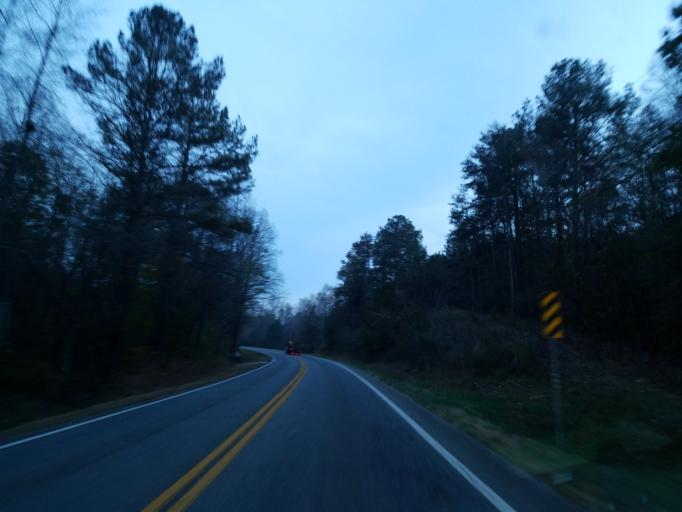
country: US
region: Georgia
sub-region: Pickens County
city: Jasper
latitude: 34.5147
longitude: -84.5665
